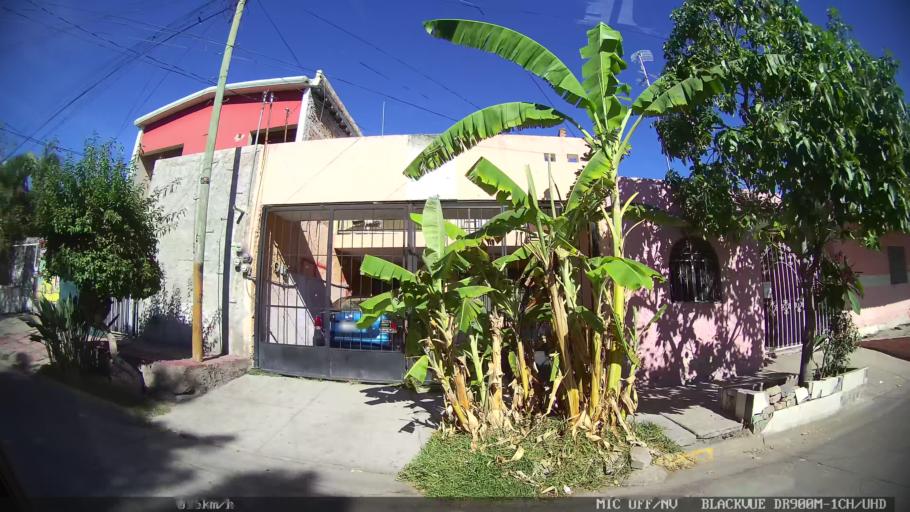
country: MX
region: Jalisco
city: Tlaquepaque
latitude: 20.6903
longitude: -103.2718
